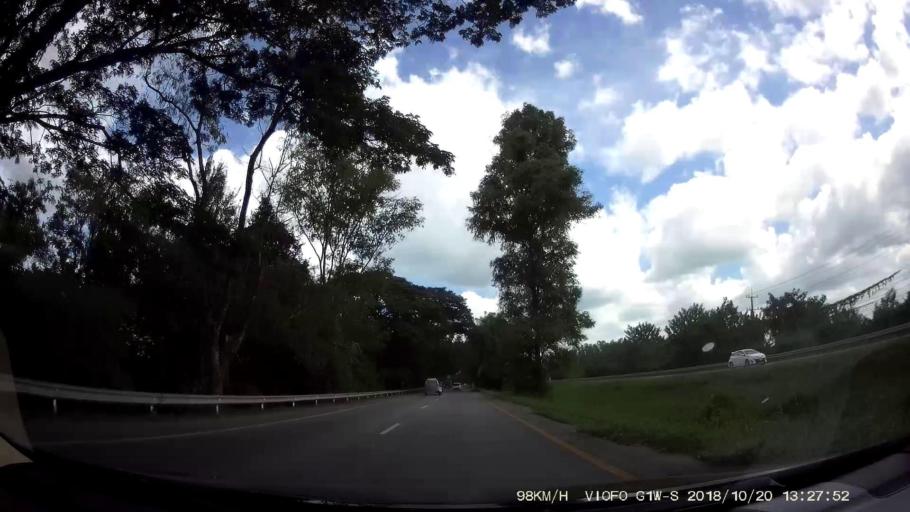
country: TH
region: Chaiyaphum
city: Khon San
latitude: 16.5920
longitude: 101.9673
